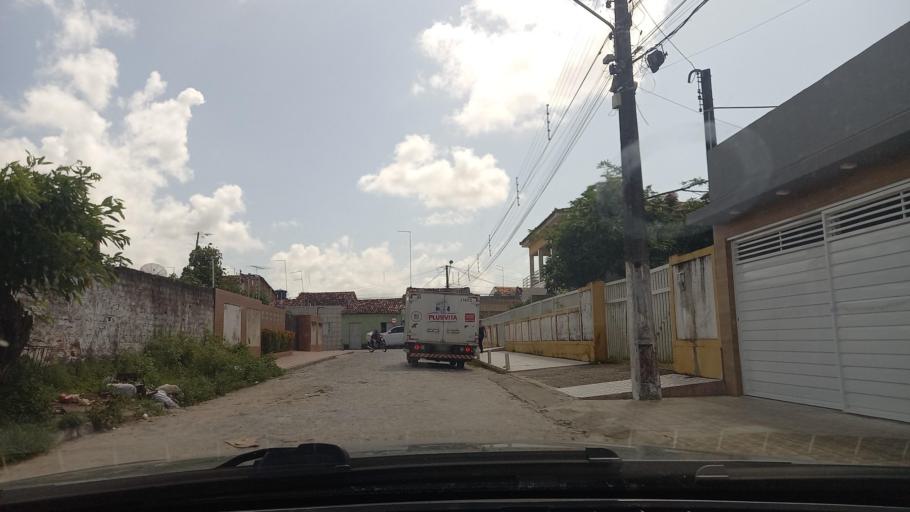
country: BR
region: Pernambuco
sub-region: Goiana
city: Goiana
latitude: -7.5619
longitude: -34.9978
